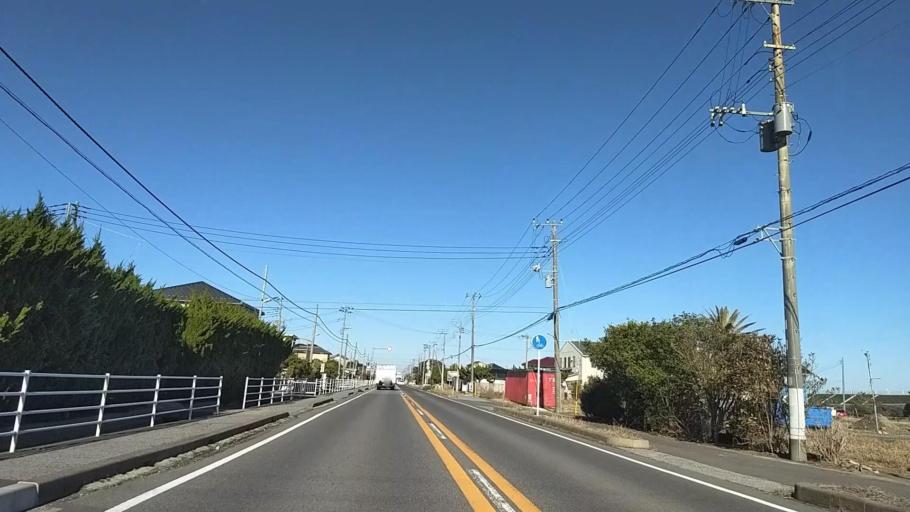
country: JP
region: Chiba
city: Togane
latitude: 35.4883
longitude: 140.4218
